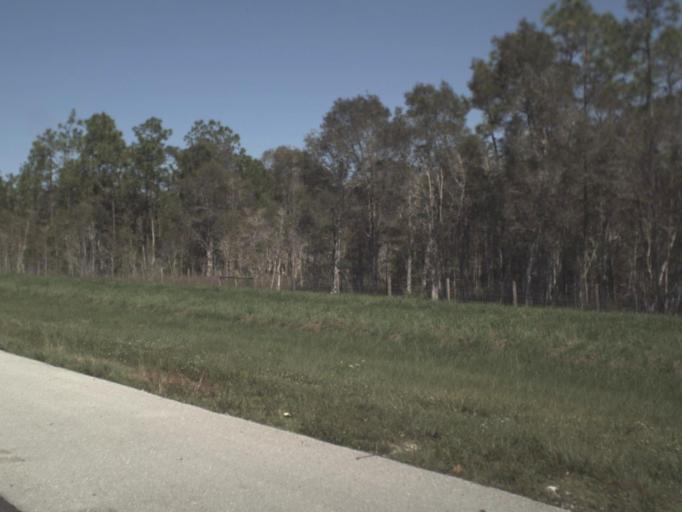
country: US
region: Florida
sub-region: Lee County
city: Estero
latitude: 26.3980
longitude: -81.7725
